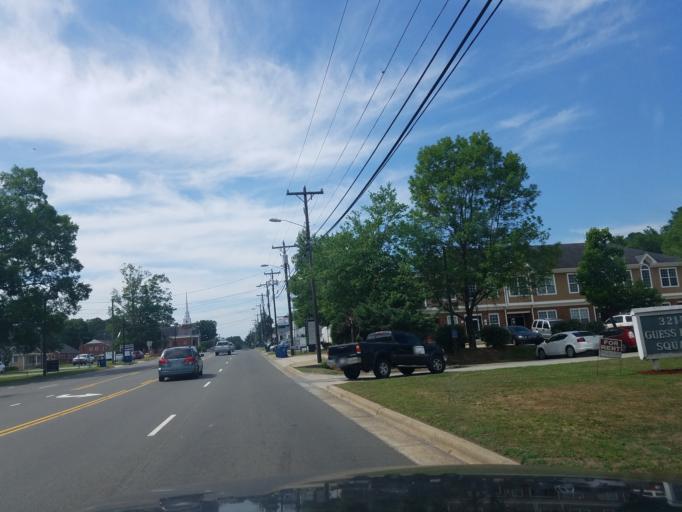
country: US
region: North Carolina
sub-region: Durham County
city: Durham
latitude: 36.0369
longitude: -78.9295
